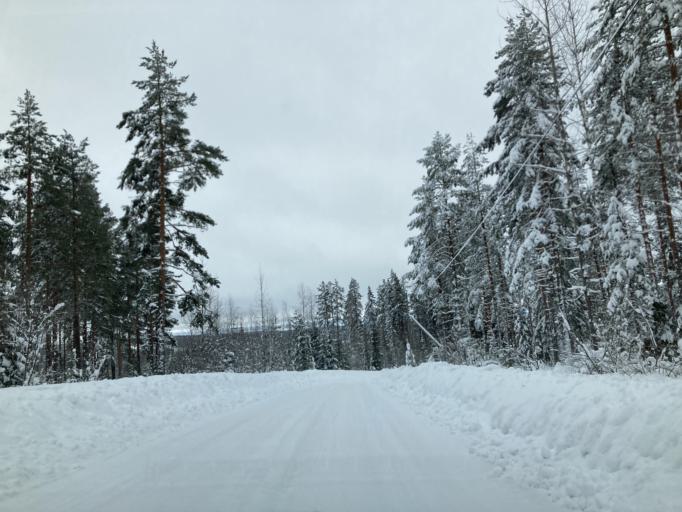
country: FI
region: Central Finland
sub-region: Jaemsae
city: Jaemsae
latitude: 61.8760
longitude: 25.3207
